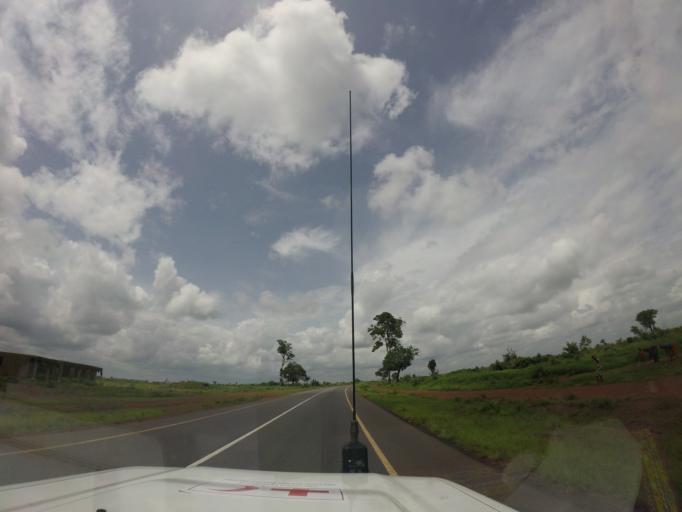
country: SL
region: Northern Province
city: Port Loko
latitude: 8.7484
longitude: -12.7577
